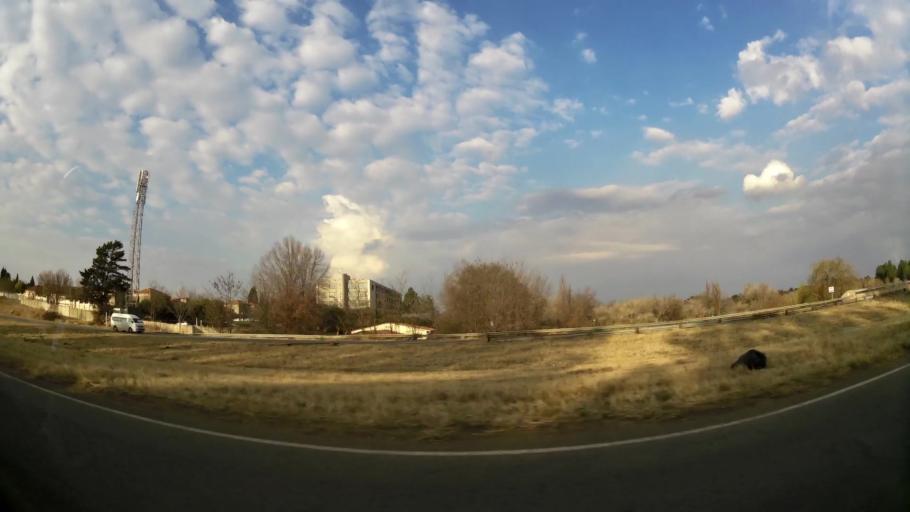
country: ZA
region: Gauteng
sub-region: Sedibeng District Municipality
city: Vanderbijlpark
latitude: -26.7490
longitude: 27.8263
